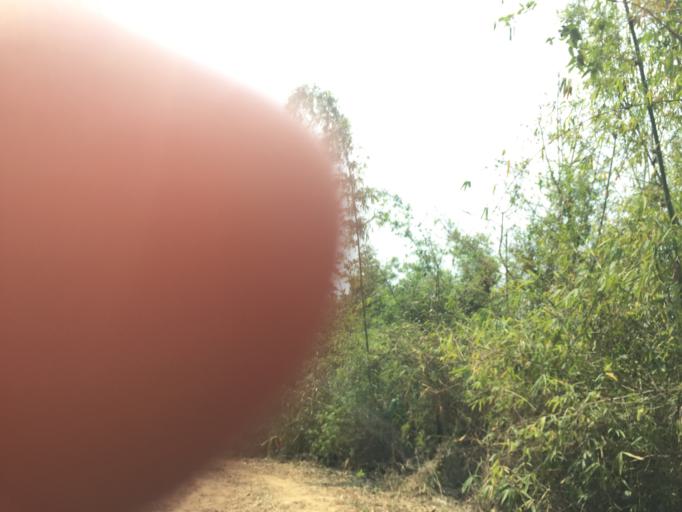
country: LA
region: Loungnamtha
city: Muang Nale
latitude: 20.6182
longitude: 101.6066
